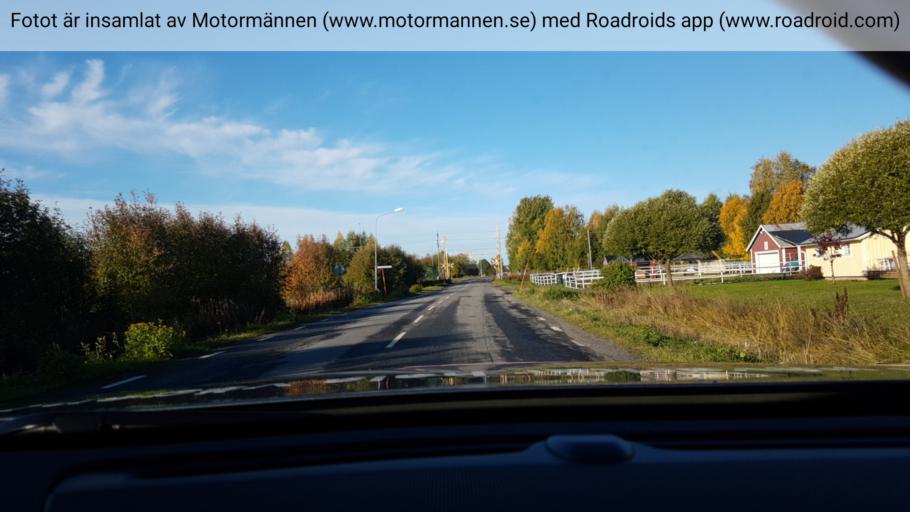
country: SE
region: Norrbotten
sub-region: Bodens Kommun
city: Boden
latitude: 65.8476
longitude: 21.7158
